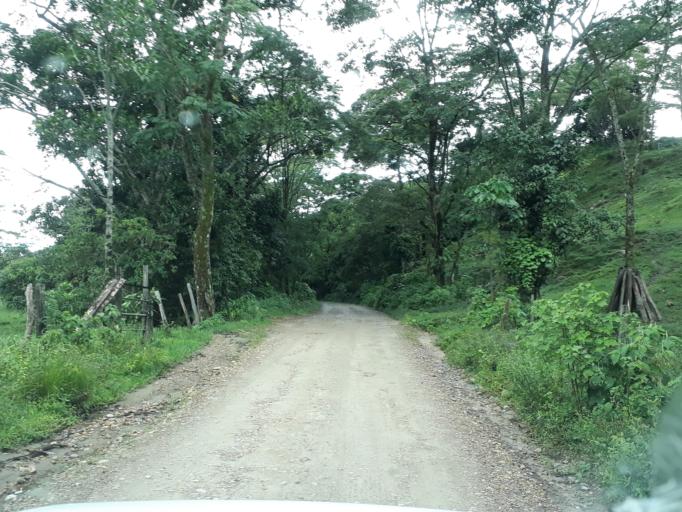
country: CO
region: Cundinamarca
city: Medina
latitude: 4.5802
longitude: -73.3781
